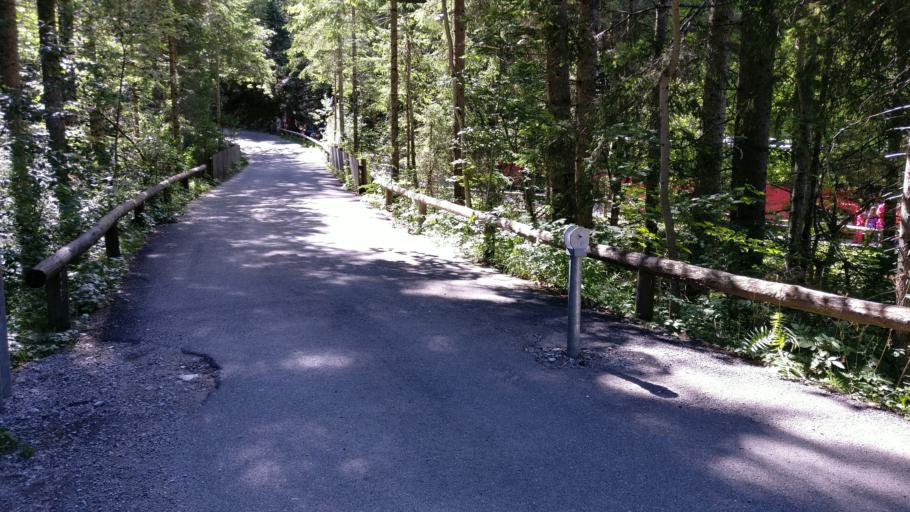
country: IT
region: Trentino-Alto Adige
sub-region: Provincia di Trento
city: Campodenno
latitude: 46.2648
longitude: 10.9547
